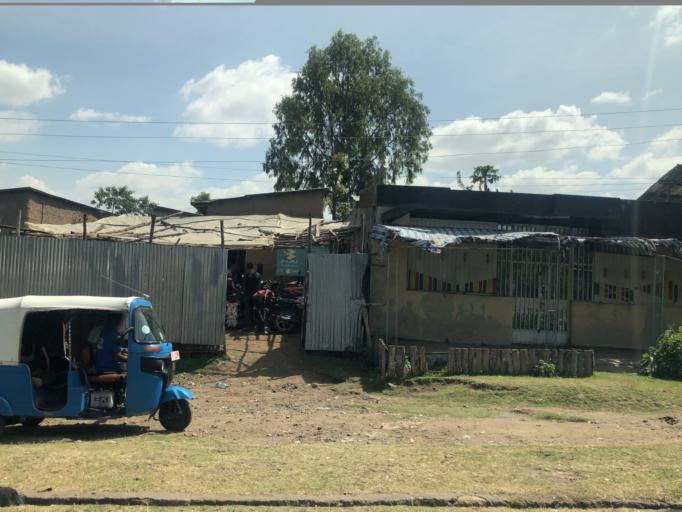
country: ET
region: Oromiya
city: Shashemene
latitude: 7.2116
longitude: 38.6182
